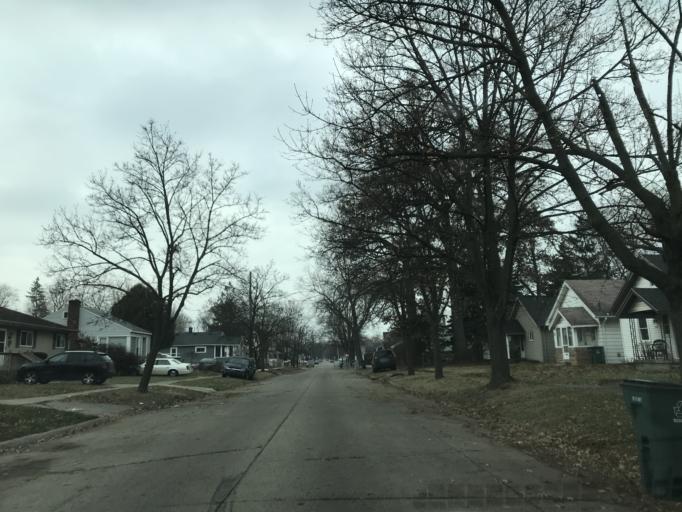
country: US
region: Michigan
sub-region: Oakland County
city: Hazel Park
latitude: 42.4502
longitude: -83.0982
